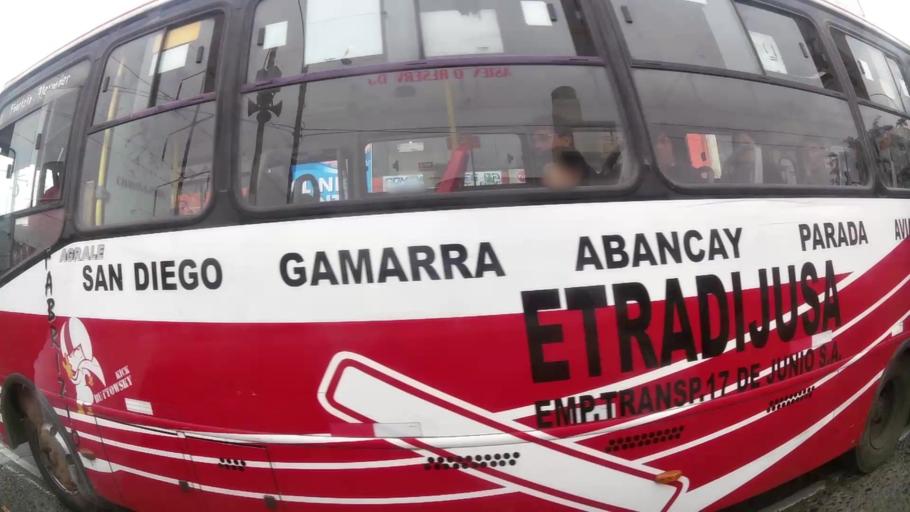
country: PE
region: Lima
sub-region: Lima
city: Independencia
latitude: -11.9763
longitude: -77.0832
